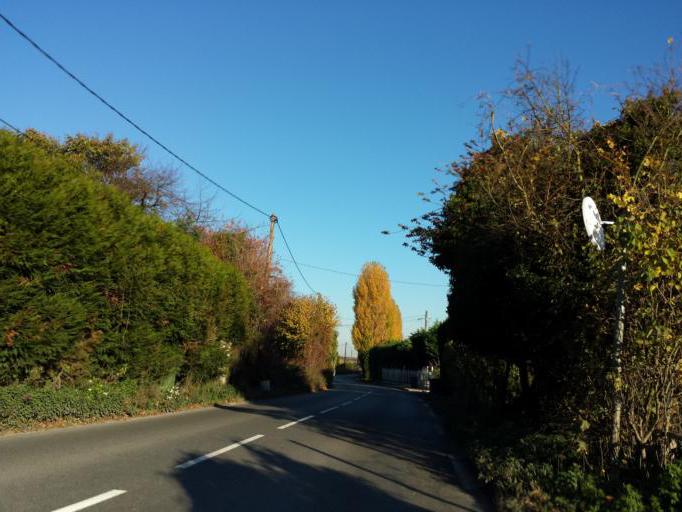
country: FR
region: Ile-de-France
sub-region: Departement du Val-d'Oise
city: Ecouen
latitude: 49.0230
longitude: 2.3900
